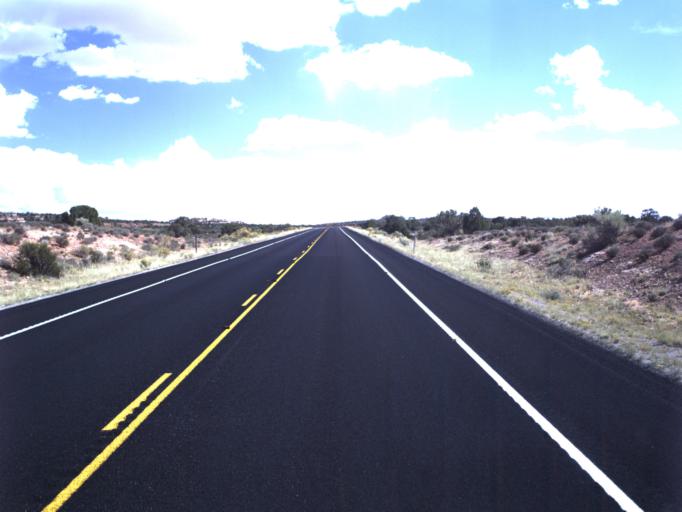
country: US
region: Utah
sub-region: Grand County
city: Moab
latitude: 38.5910
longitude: -109.8087
